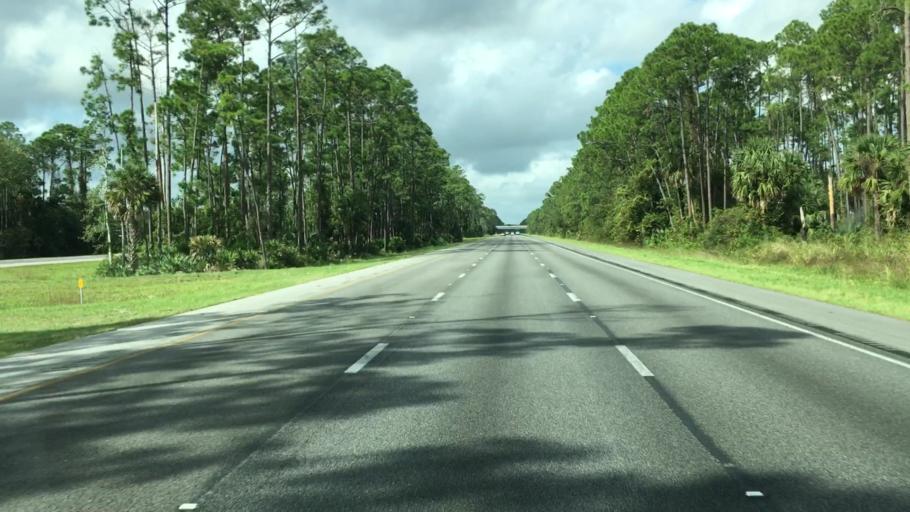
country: US
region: Florida
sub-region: Volusia County
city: Port Orange
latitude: 29.1177
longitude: -81.0398
